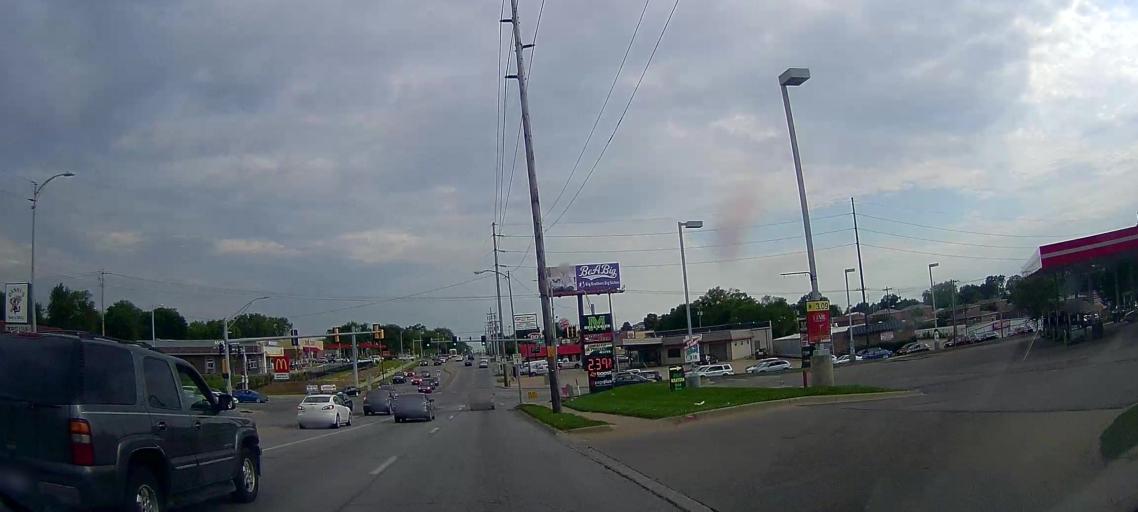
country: US
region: Nebraska
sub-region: Douglas County
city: Ralston
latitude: 41.2782
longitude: -96.0239
